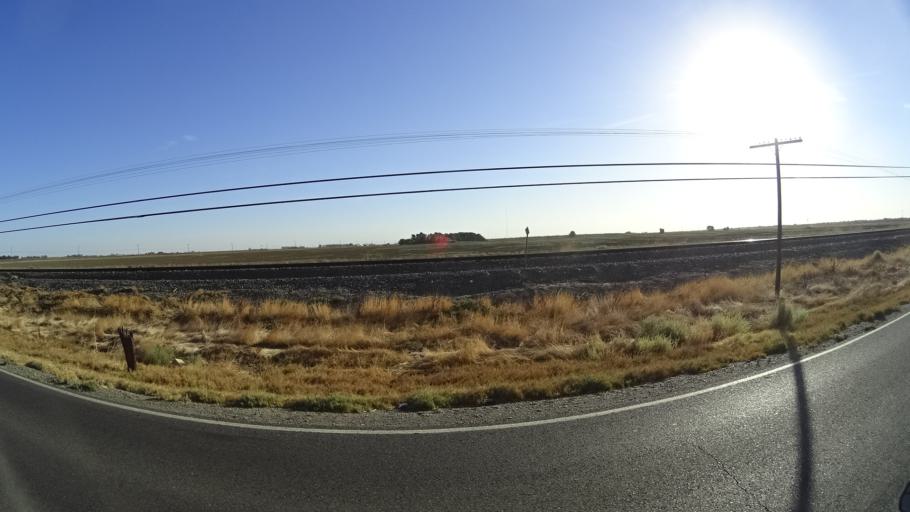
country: US
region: California
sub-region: Yolo County
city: Davis
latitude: 38.5875
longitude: -121.7517
